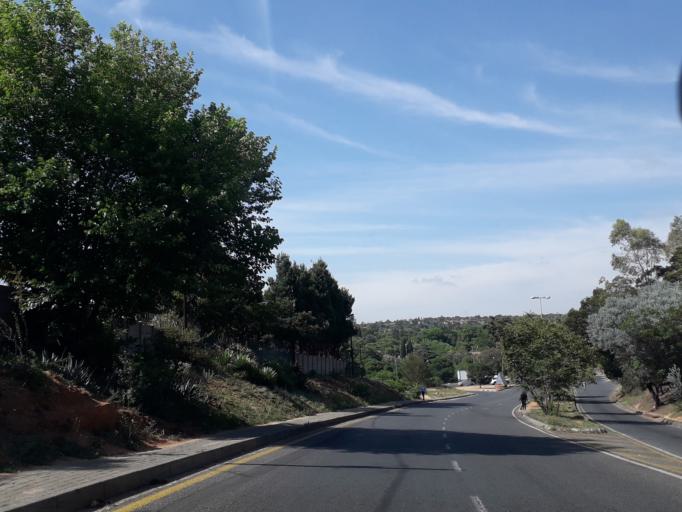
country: ZA
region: Gauteng
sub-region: West Rand District Municipality
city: Muldersdriseloop
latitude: -26.0669
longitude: 27.9694
